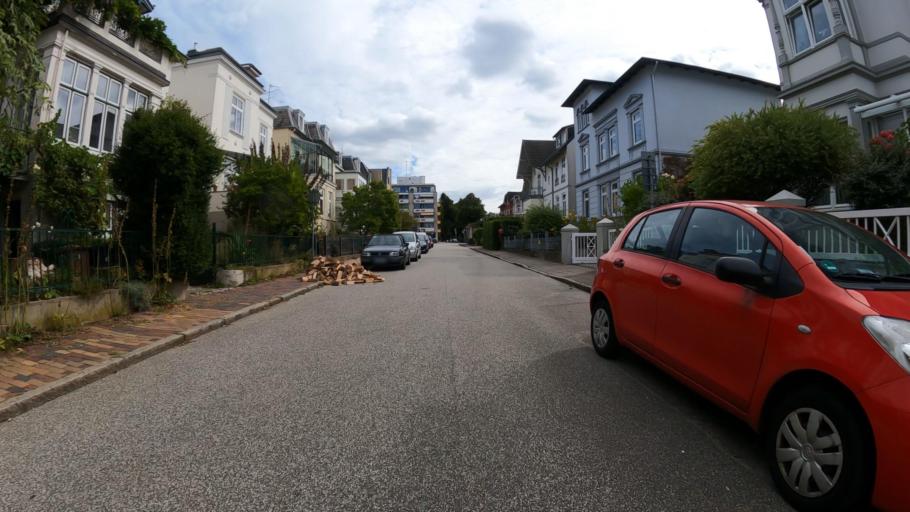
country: DE
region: Schleswig-Holstein
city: Luebeck
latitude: 53.8547
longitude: 10.6868
